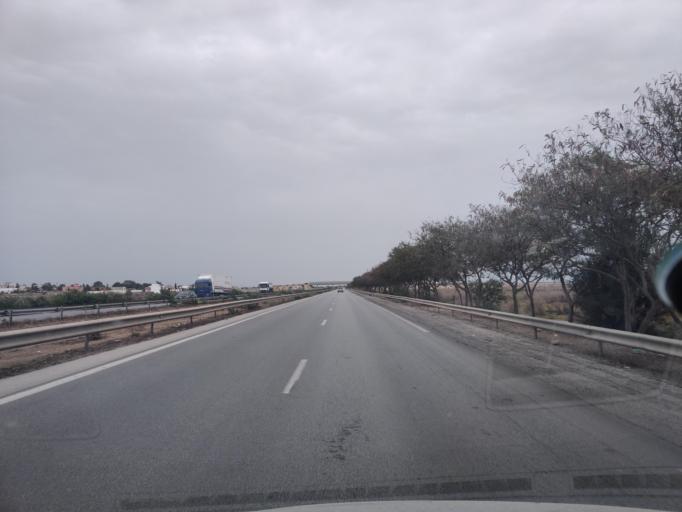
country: TN
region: Susah
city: Harqalah
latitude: 36.1594
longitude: 10.4191
